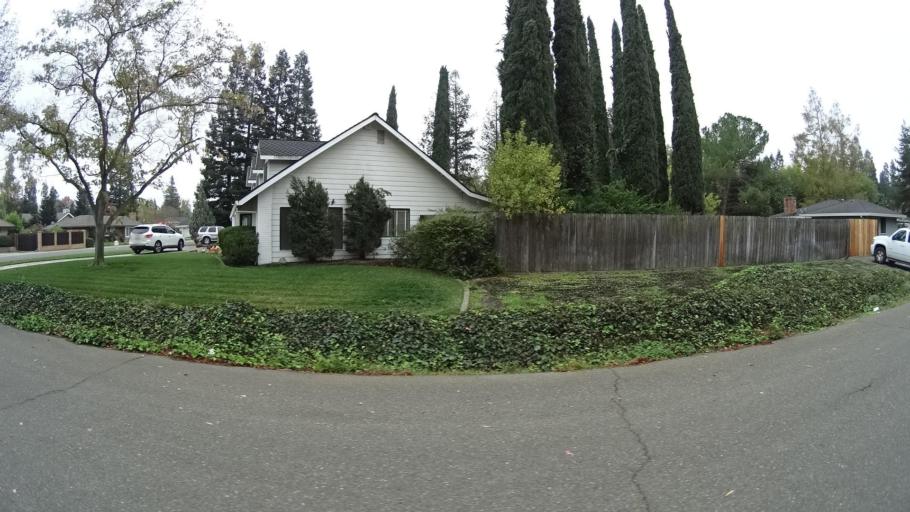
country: US
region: California
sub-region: Sacramento County
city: Elk Grove
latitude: 38.4137
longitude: -121.3628
